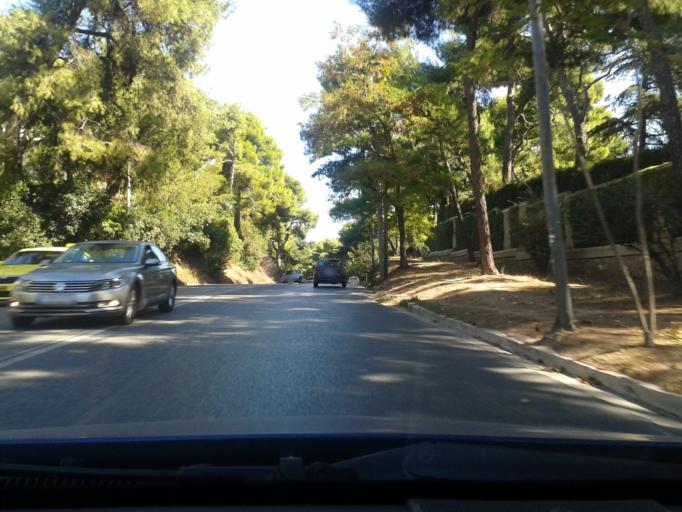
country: GR
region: Attica
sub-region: Nomarchia Athinas
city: Ekali
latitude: 38.1107
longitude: 23.8426
